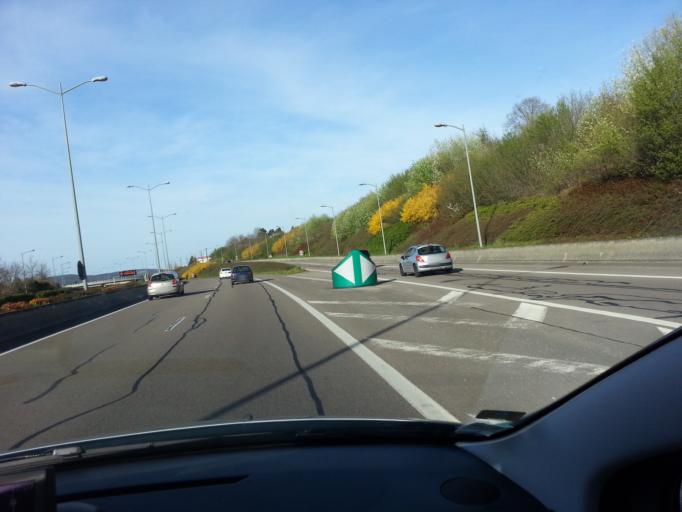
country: FR
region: Franche-Comte
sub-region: Departement du Doubs
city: Besancon
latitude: 47.2590
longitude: 6.0029
